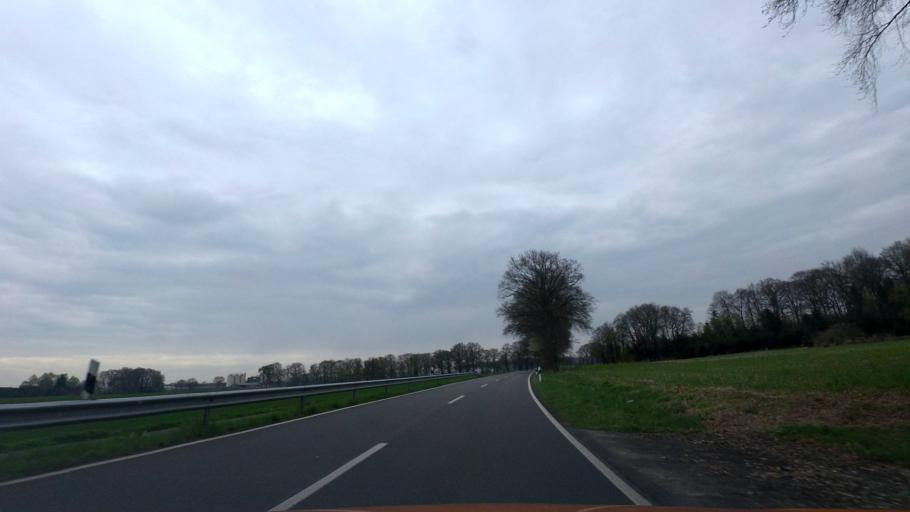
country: DE
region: Lower Saxony
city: Cloppenburg
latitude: 52.8051
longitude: 8.0262
